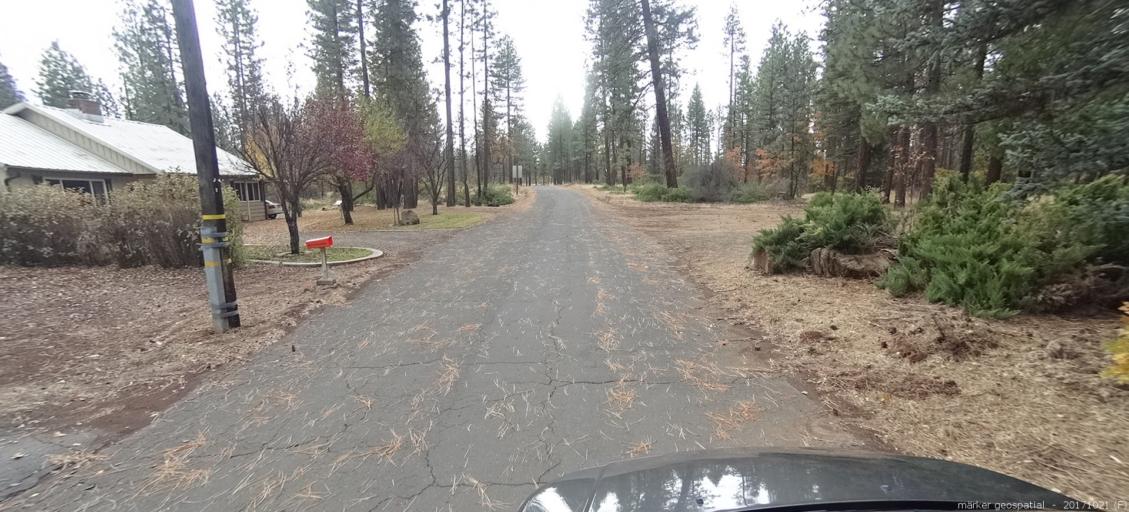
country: US
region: California
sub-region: Shasta County
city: Burney
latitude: 40.9976
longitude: -121.6334
